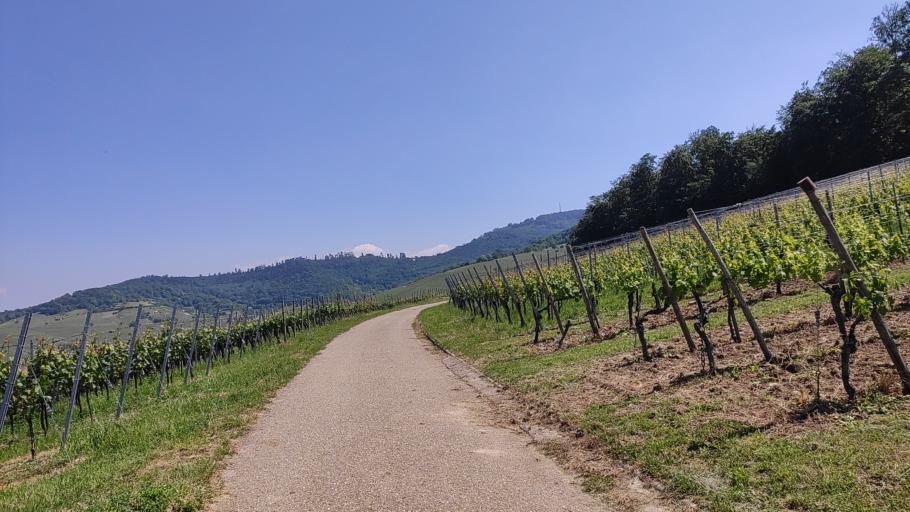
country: DE
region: Baden-Wuerttemberg
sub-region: Freiburg Region
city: Ebringen
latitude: 47.9505
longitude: 7.7688
